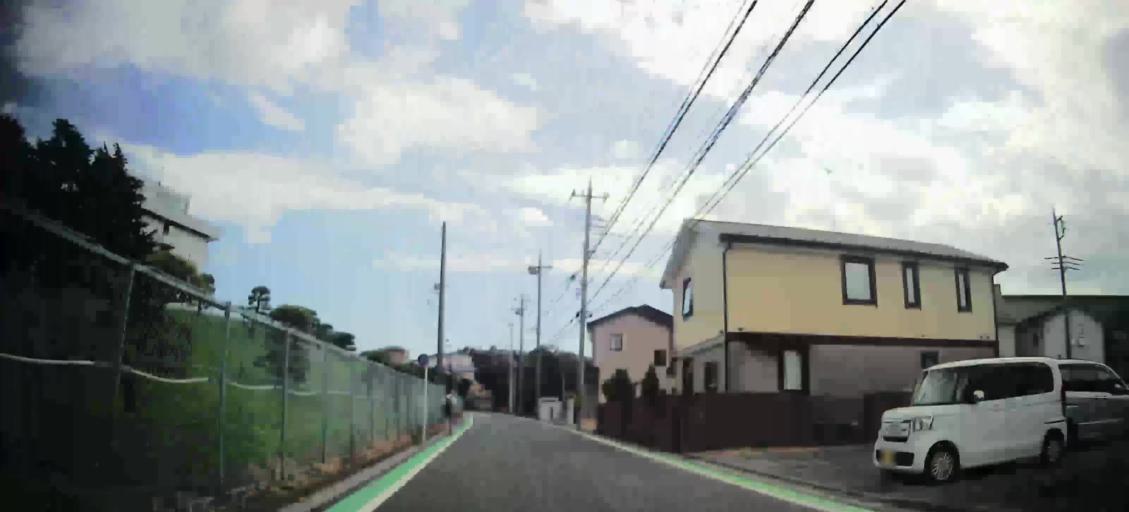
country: JP
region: Kanagawa
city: Yokohama
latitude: 35.4862
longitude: 139.5755
